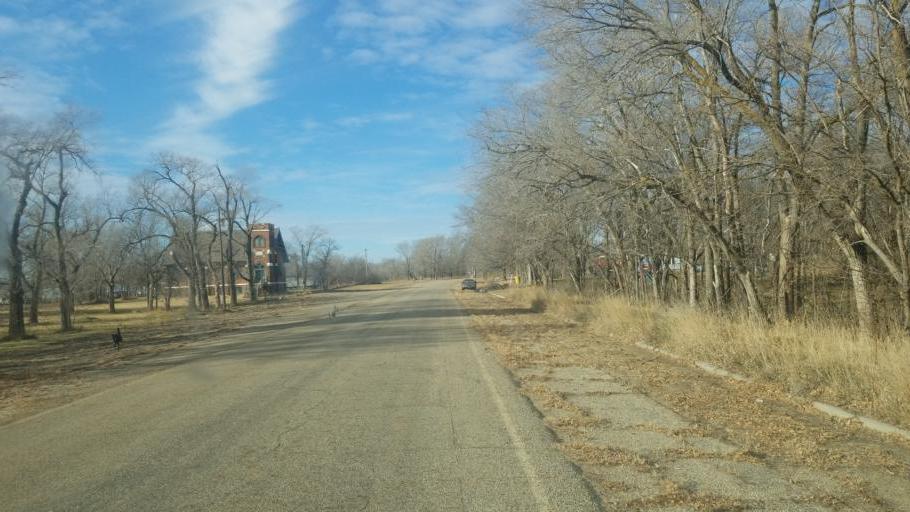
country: US
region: South Dakota
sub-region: Charles Mix County
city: Wagner
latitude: 42.9228
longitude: -98.3874
